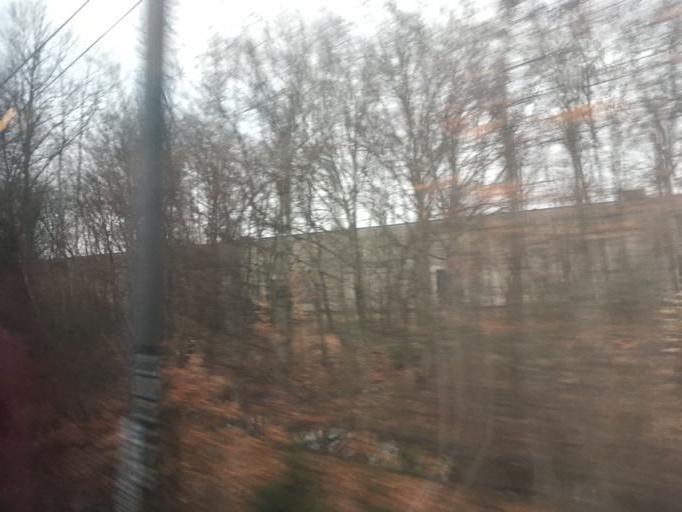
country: US
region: Massachusetts
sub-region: Bristol County
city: Mansfield Center
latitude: 42.0198
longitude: -71.2292
